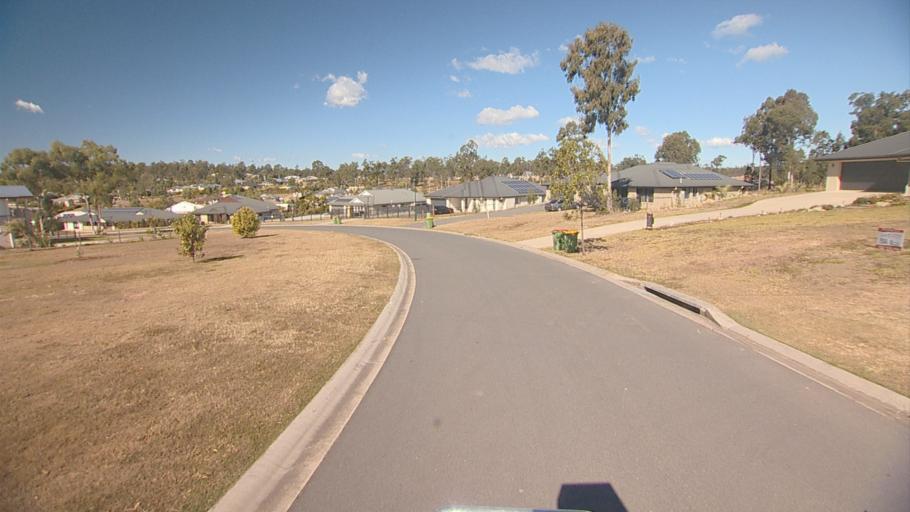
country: AU
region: Queensland
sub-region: Logan
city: North Maclean
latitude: -27.7559
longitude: 152.9465
